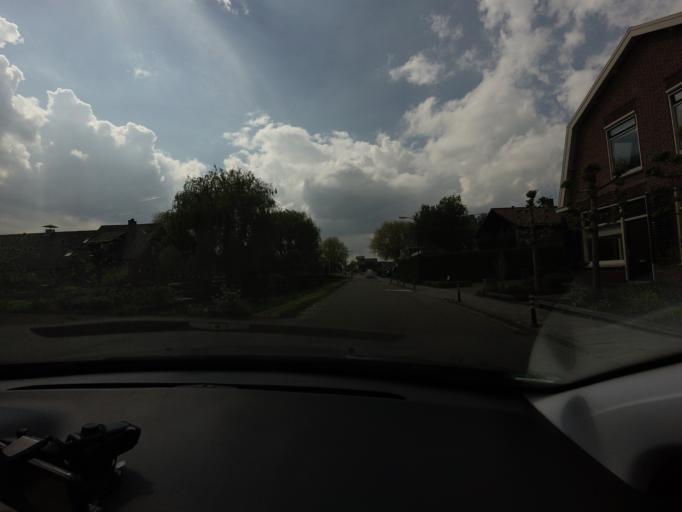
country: NL
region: Utrecht
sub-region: Gemeente De Ronde Venen
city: Mijdrecht
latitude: 52.1956
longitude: 4.9080
